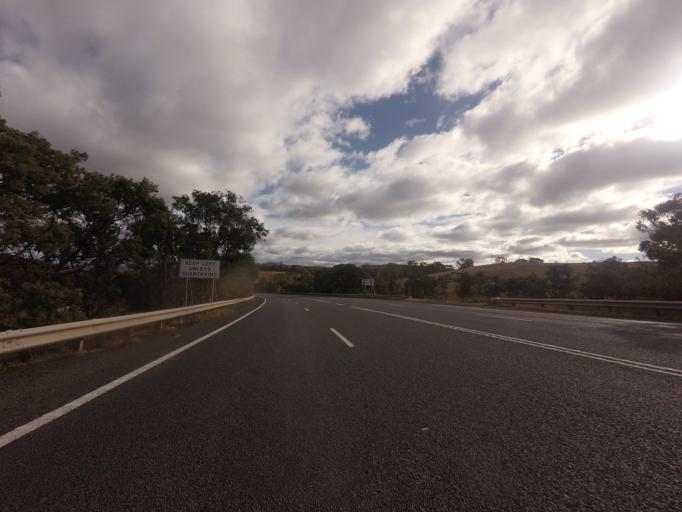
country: AU
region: Tasmania
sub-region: Brighton
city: Bridgewater
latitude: -42.4491
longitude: 147.2080
